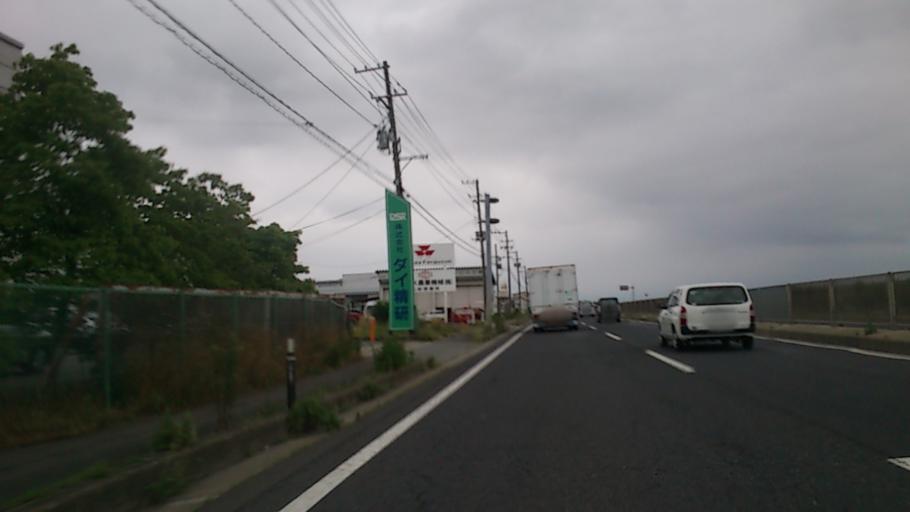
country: JP
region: Yamagata
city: Higashine
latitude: 38.4150
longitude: 140.3749
